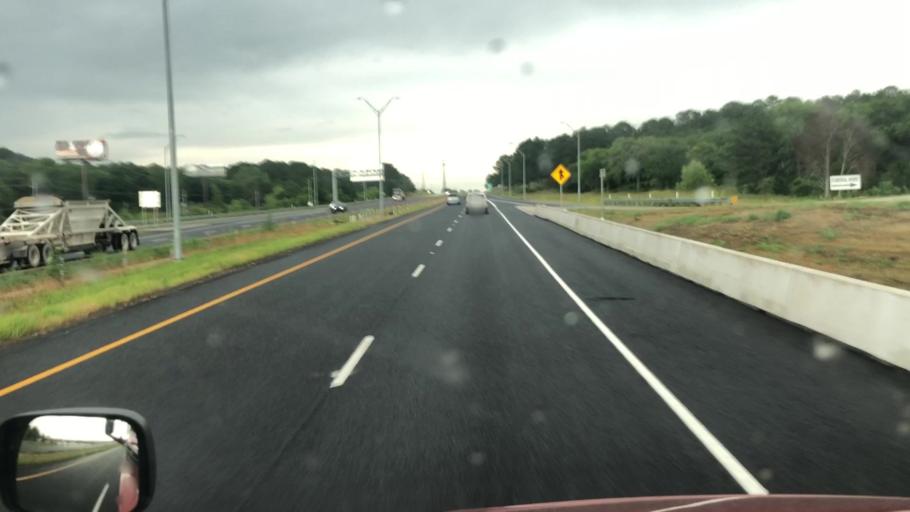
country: US
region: Texas
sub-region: Bastrop County
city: Bastrop
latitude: 30.1050
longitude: -97.3044
